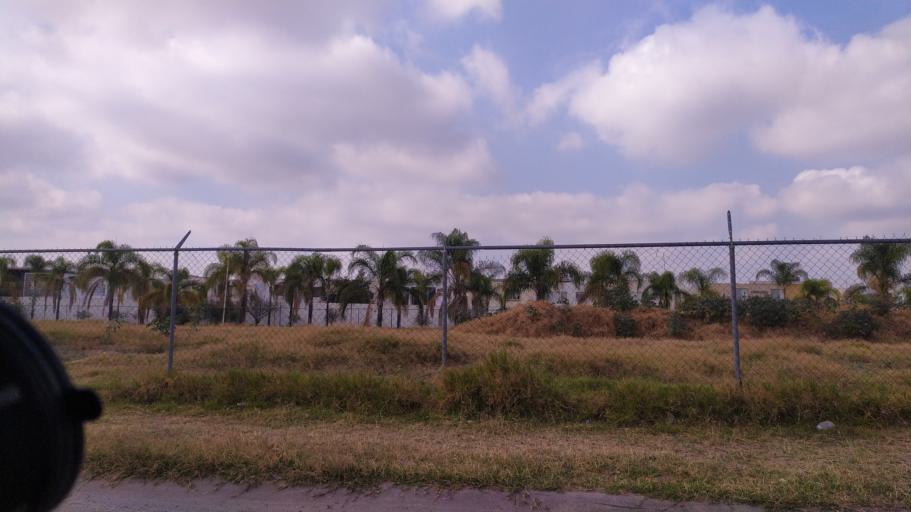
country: MX
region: Jalisco
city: Zapopan2
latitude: 20.7039
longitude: -103.4448
